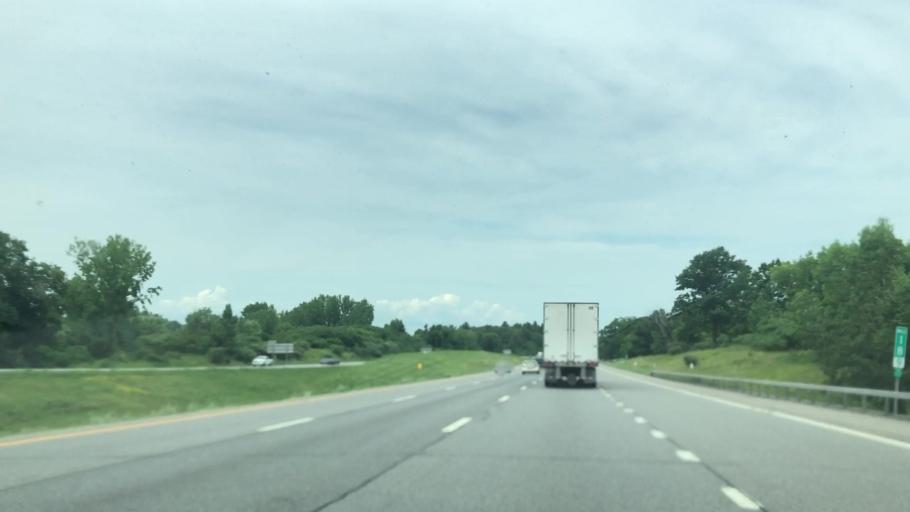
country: US
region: New York
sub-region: Saratoga County
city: Country Knolls
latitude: 42.9402
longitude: -73.8045
